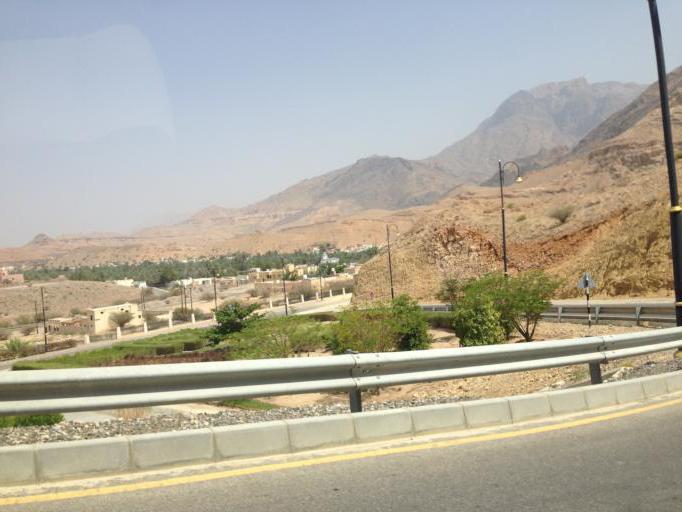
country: OM
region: Ash Sharqiyah
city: Ibra'
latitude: 23.0892
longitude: 58.8500
